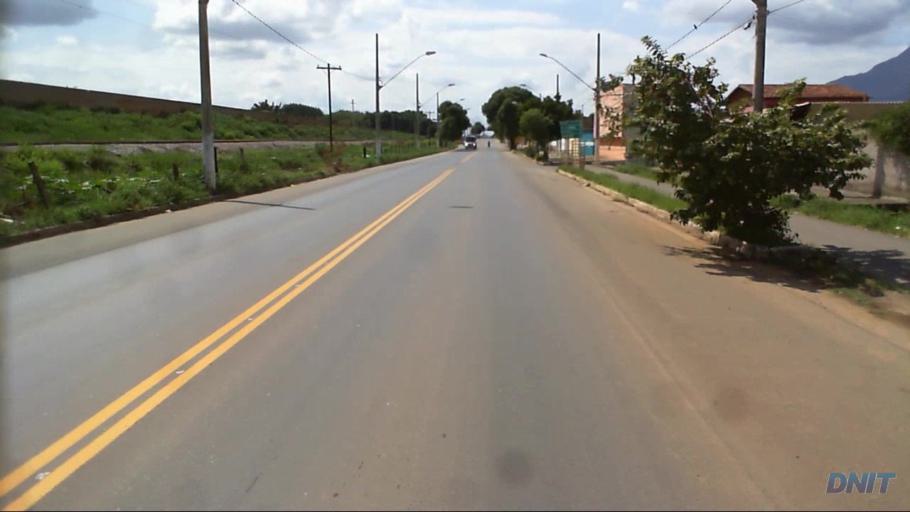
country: BR
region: Minas Gerais
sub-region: Governador Valadares
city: Governador Valadares
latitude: -18.9085
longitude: -41.9933
